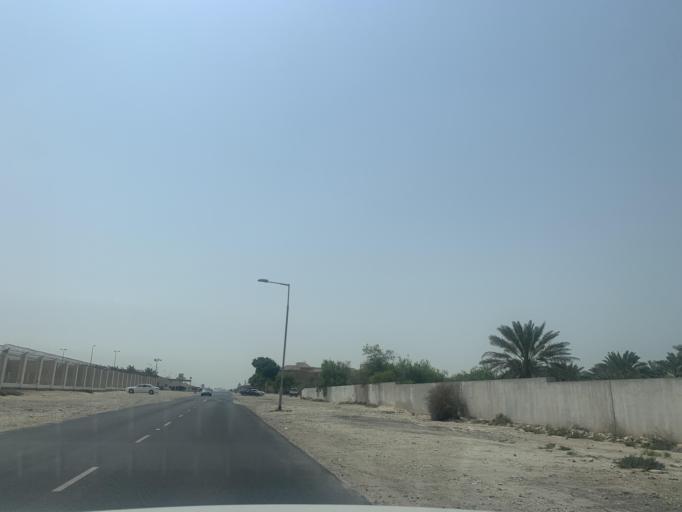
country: BH
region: Central Governorate
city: Madinat Hamad
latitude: 26.1533
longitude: 50.4719
